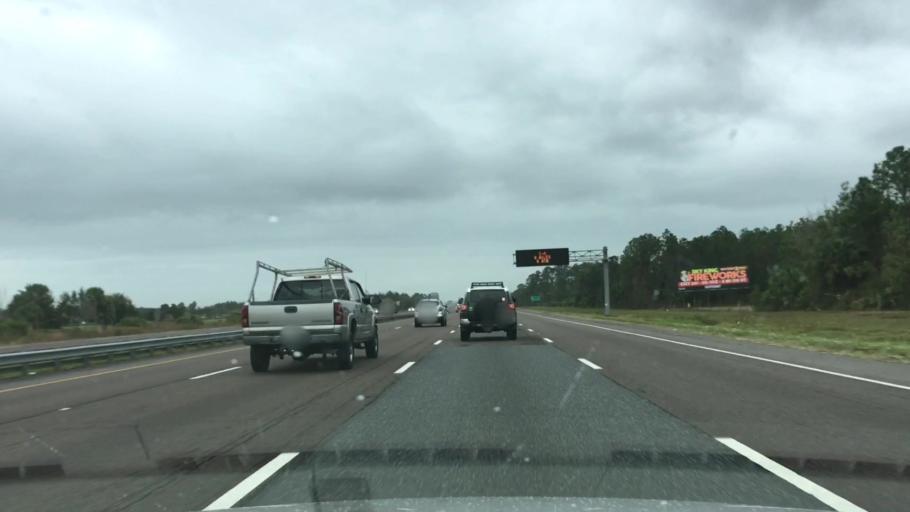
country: US
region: Florida
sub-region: Volusia County
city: Ormond Beach
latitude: 29.2454
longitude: -81.1124
